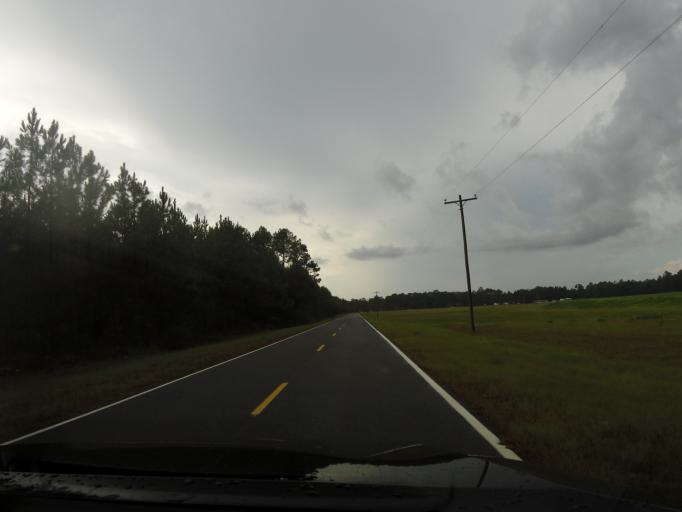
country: US
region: Georgia
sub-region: Wayne County
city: Jesup
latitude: 31.5534
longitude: -81.8893
